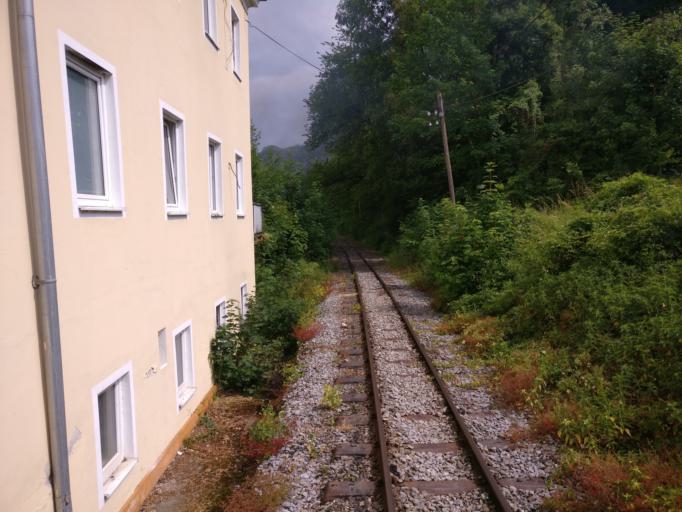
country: AT
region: Upper Austria
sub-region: Politischer Bezirk Steyr-Land
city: Sierning
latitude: 48.0329
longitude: 14.3379
